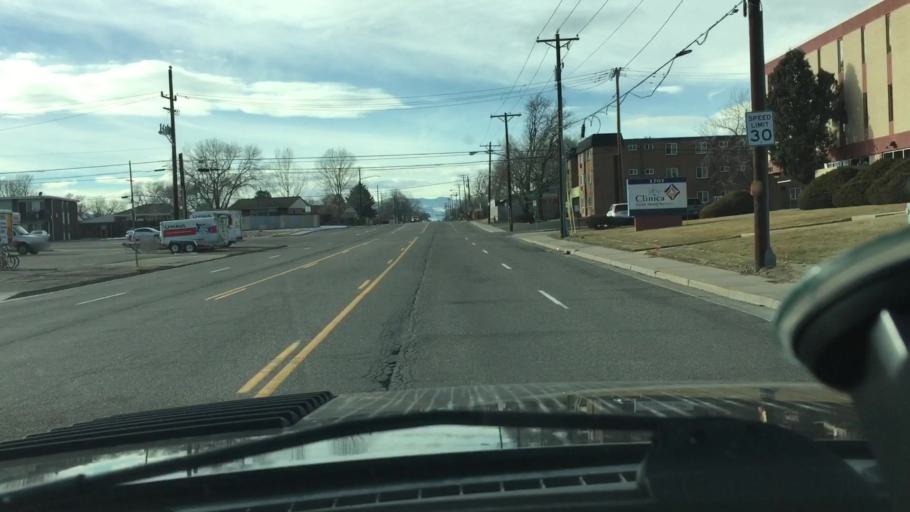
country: US
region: Colorado
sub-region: Adams County
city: Twin Lakes
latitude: 39.8273
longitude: -105.0070
